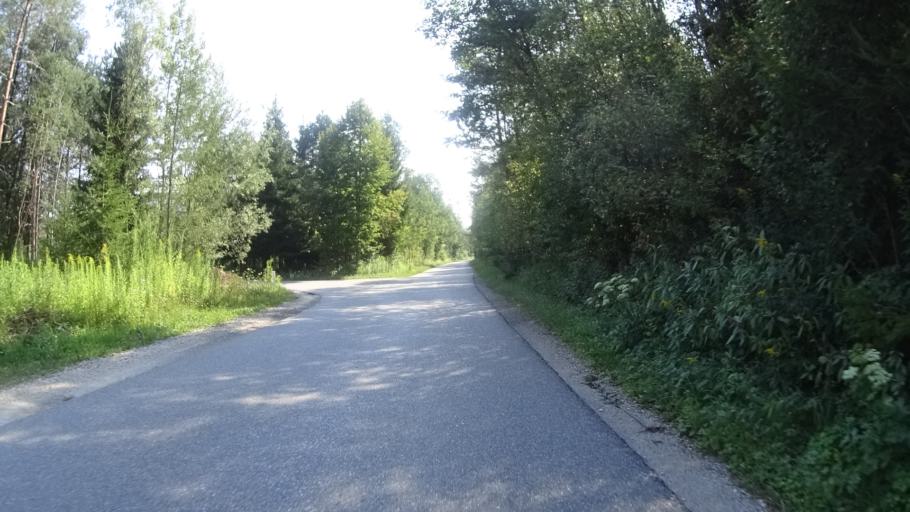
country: AT
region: Carinthia
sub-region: Politischer Bezirk Klagenfurt Land
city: Grafenstein
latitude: 46.5590
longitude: 14.4190
